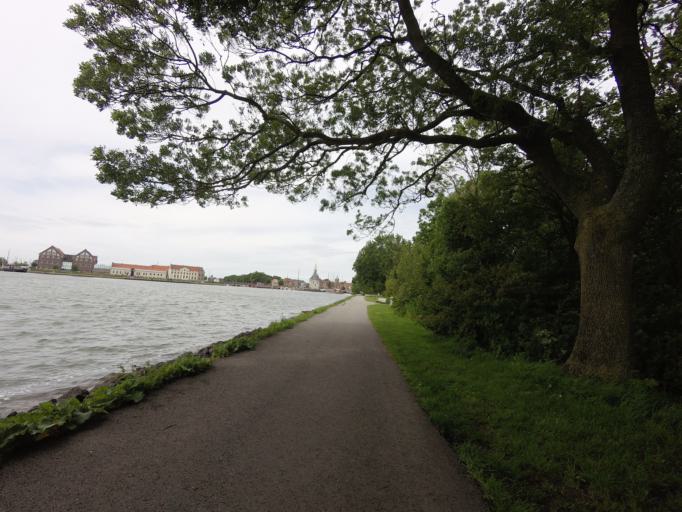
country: NL
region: North Holland
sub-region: Gemeente Hoorn
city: Hoorn
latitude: 52.6353
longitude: 5.0675
